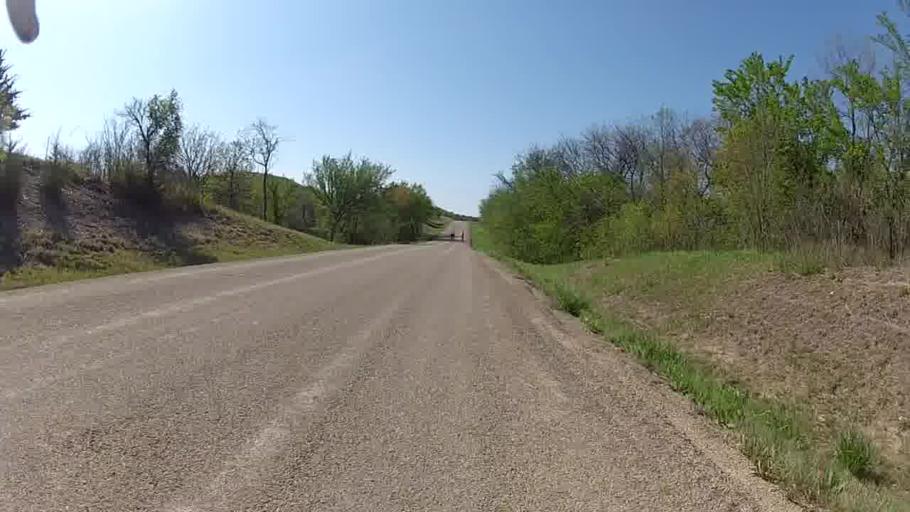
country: US
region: Kansas
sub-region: Riley County
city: Ogden
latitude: 38.9985
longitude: -96.6675
